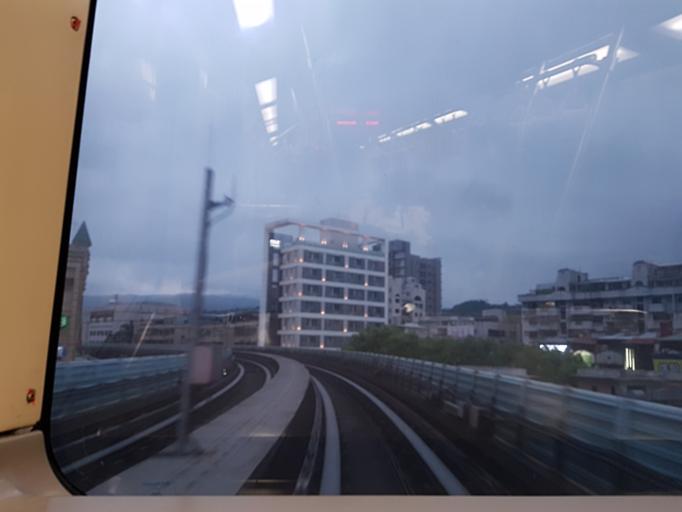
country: TW
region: Taipei
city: Taipei
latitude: 25.0689
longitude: 121.6122
